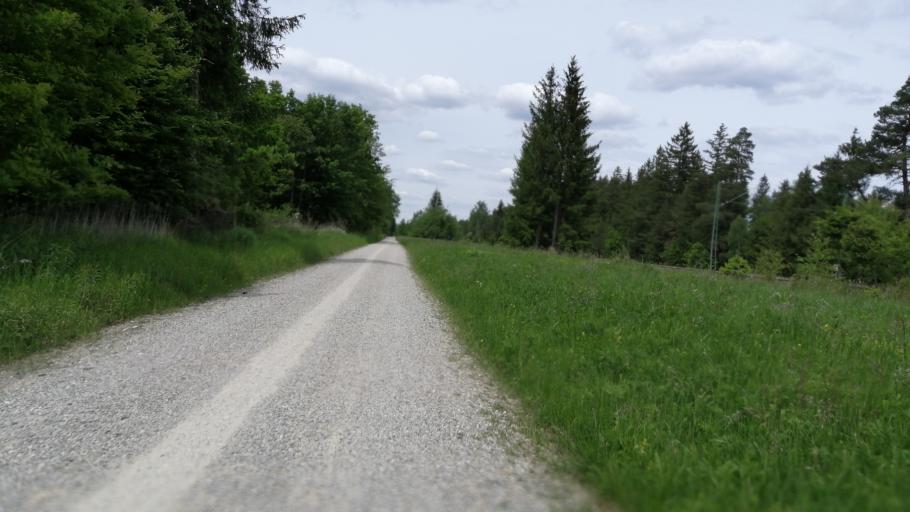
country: DE
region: Bavaria
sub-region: Upper Bavaria
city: Oberhaching
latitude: 48.0557
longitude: 11.5662
